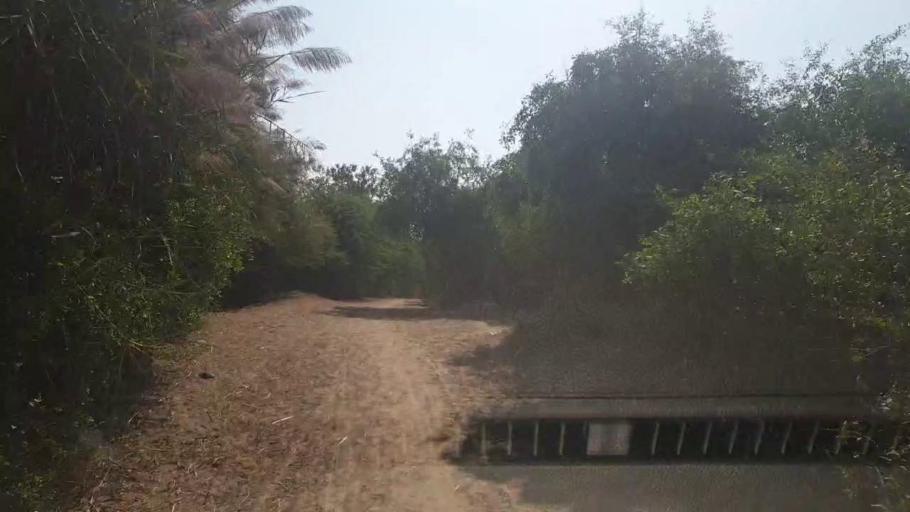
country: PK
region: Sindh
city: Badin
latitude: 24.7142
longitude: 68.9000
